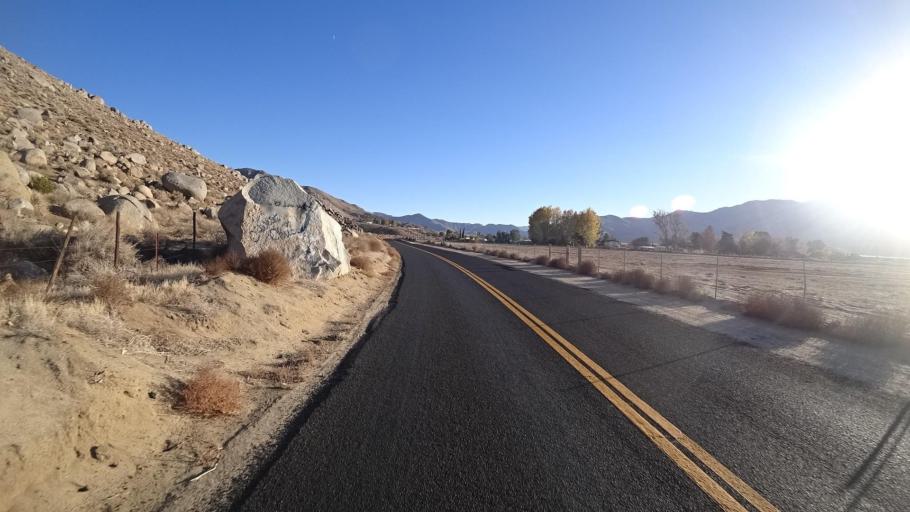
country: US
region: California
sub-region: Kern County
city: Weldon
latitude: 35.6467
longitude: -118.2511
